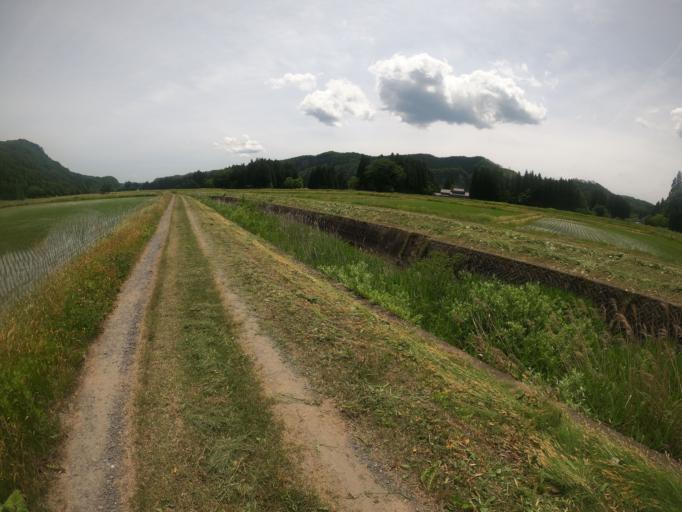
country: JP
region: Iwate
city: Ichinoseki
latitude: 38.9762
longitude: 140.9561
